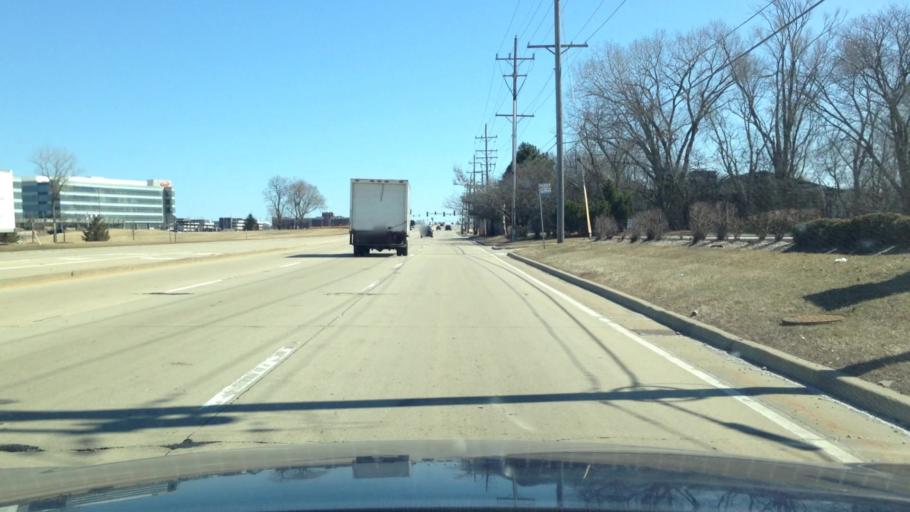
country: US
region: Illinois
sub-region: Lake County
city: Riverwoods
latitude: 42.1529
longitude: -87.8831
